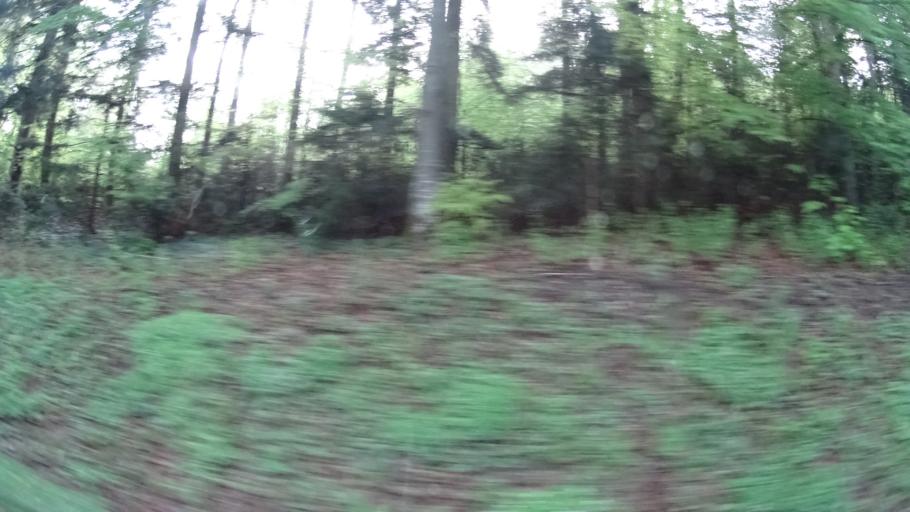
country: DE
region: Baden-Wuerttemberg
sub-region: Karlsruhe Region
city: Empfingen
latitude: 48.4364
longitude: 8.7709
